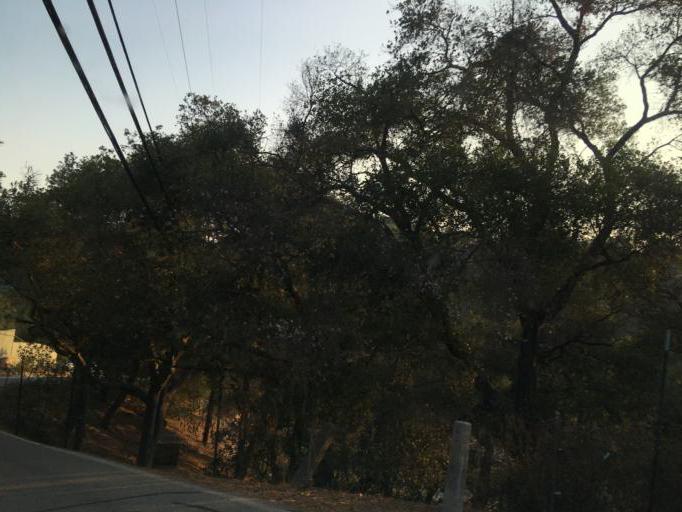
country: US
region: California
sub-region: Los Angeles County
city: Topanga
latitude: 34.0805
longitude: -118.5991
